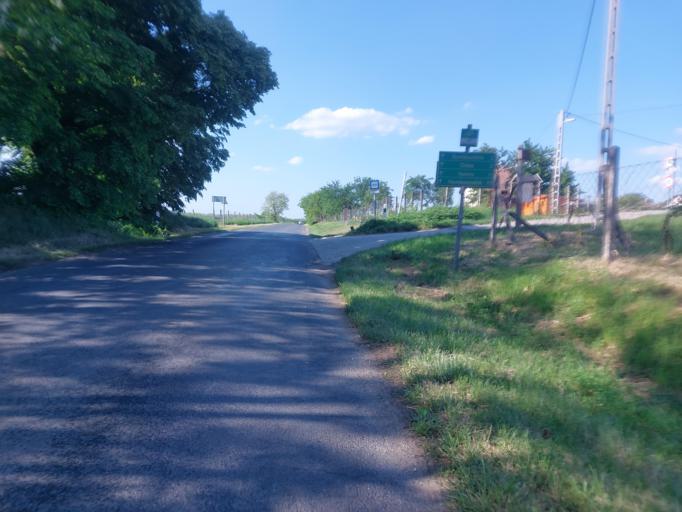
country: HU
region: Veszprem
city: Devecser
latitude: 47.1432
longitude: 17.3554
